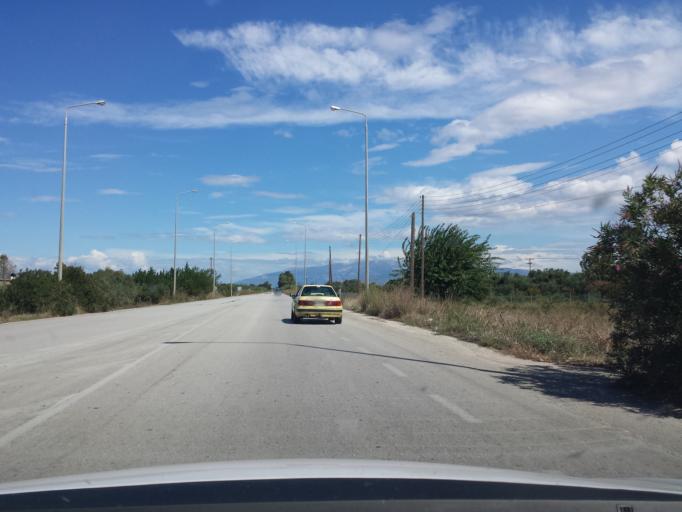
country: GR
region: West Greece
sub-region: Nomos Achaias
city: Limnokhorion
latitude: 38.1089
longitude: 21.4877
